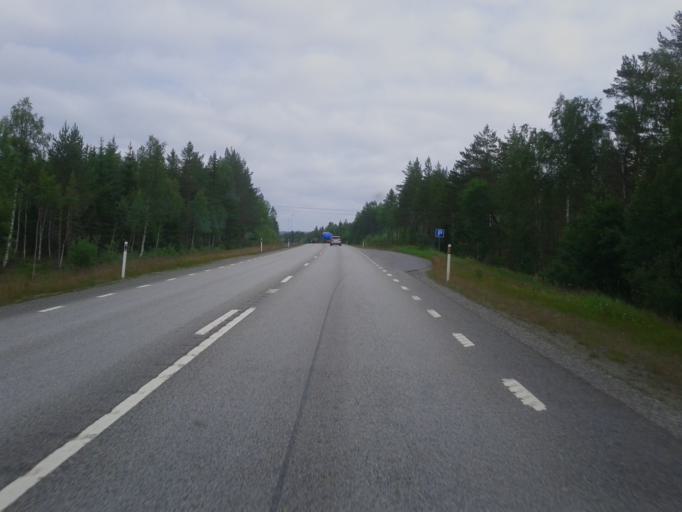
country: SE
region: Vaesterbotten
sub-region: Robertsfors Kommun
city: Robertsfors
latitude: 64.2791
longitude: 21.0623
